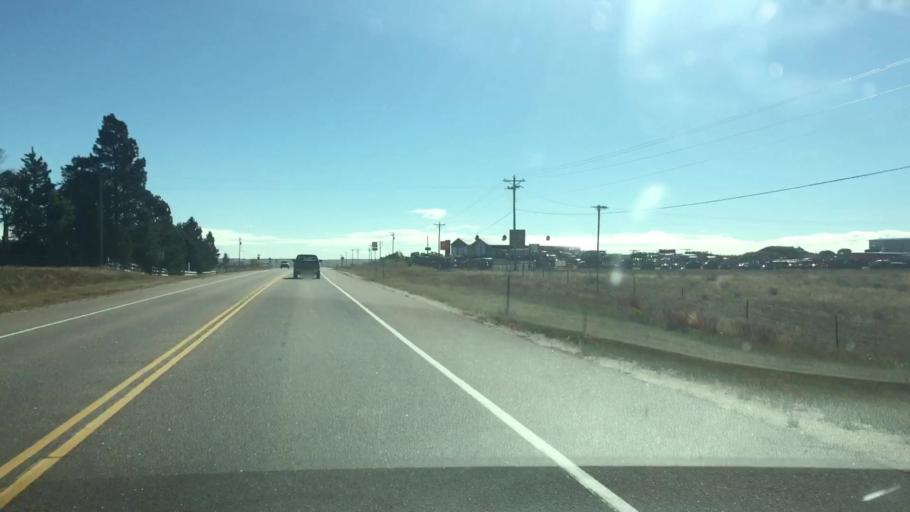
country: US
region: Colorado
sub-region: Elbert County
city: Kiowa
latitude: 39.3559
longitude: -104.5207
